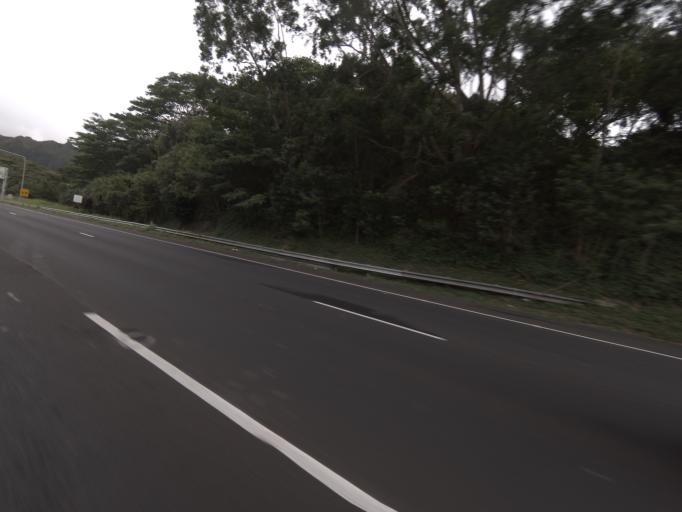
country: US
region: Hawaii
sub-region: Honolulu County
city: Kane'ohe
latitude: 21.3988
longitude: -157.8102
